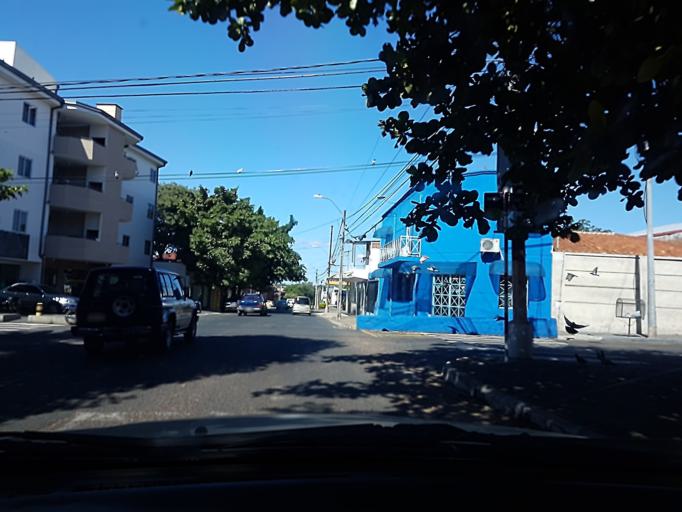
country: PY
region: Asuncion
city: Asuncion
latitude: -25.3057
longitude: -57.6015
